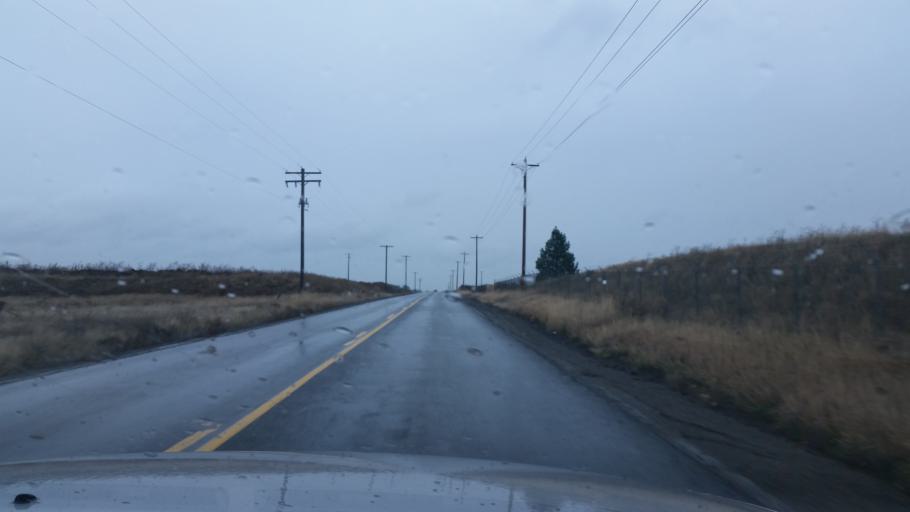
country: US
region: Washington
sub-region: Spokane County
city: Airway Heights
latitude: 47.6794
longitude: -117.5611
